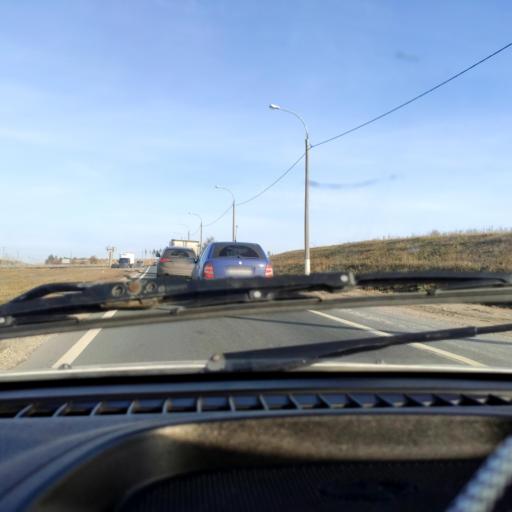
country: RU
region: Samara
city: Zhigulevsk
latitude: 53.4963
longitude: 49.5369
